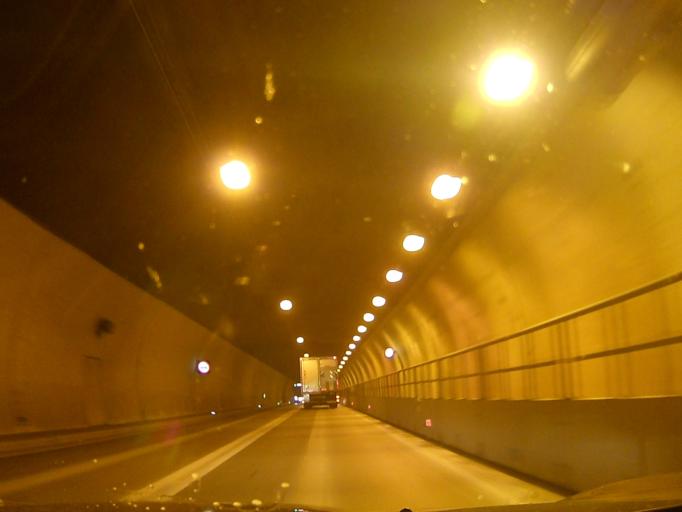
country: AT
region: Salzburg
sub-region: Politischer Bezirk Zell am See
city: Lend
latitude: 47.2812
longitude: 13.0749
